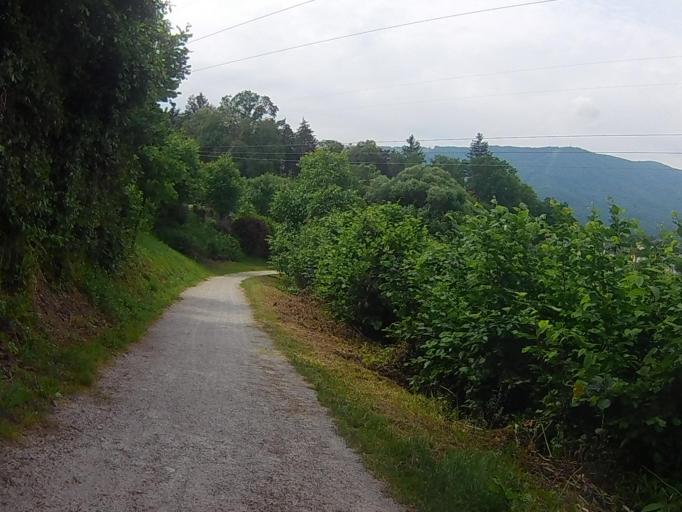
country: SI
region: Maribor
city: Pekre
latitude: 46.5494
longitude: 15.6046
